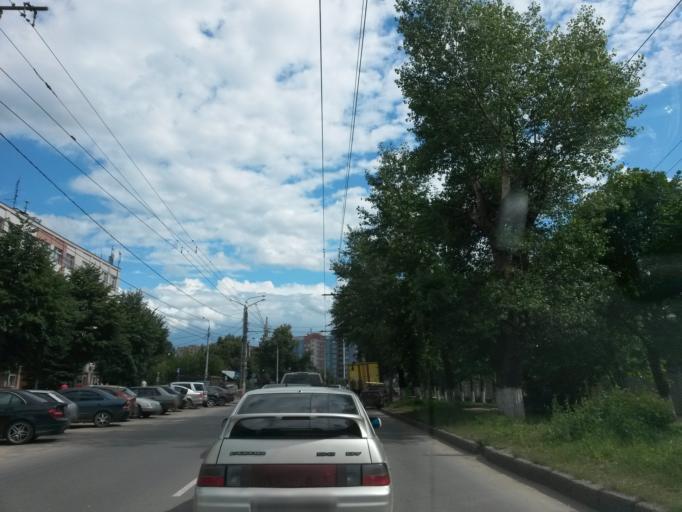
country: RU
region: Ivanovo
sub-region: Gorod Ivanovo
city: Ivanovo
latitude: 56.9960
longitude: 40.9613
